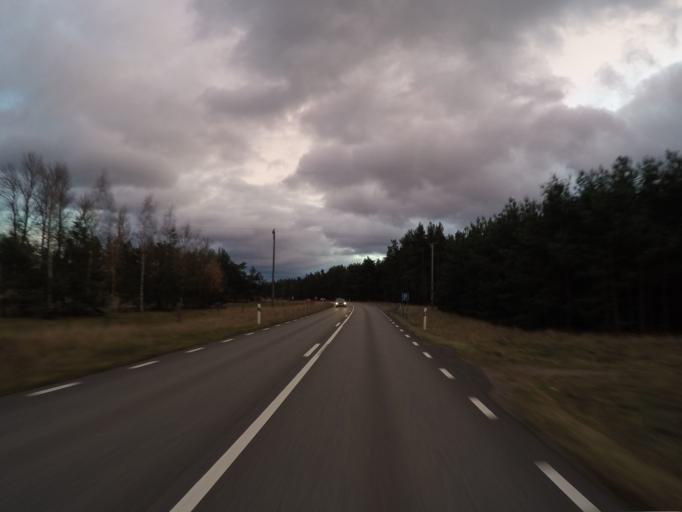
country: SE
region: Skane
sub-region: Kristianstads Kommun
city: Degeberga
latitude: 55.8803
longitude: 14.0868
